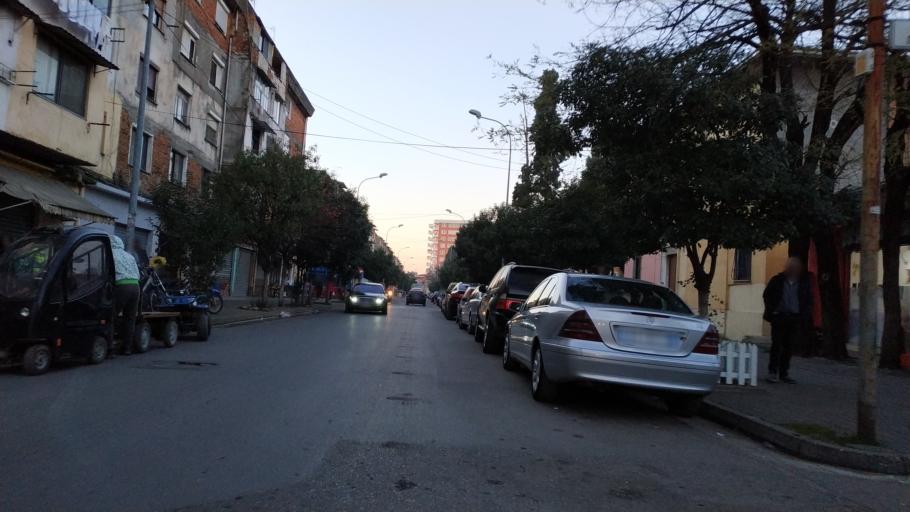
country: AL
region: Shkoder
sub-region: Rrethi i Shkodres
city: Shkoder
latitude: 42.0735
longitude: 19.5203
